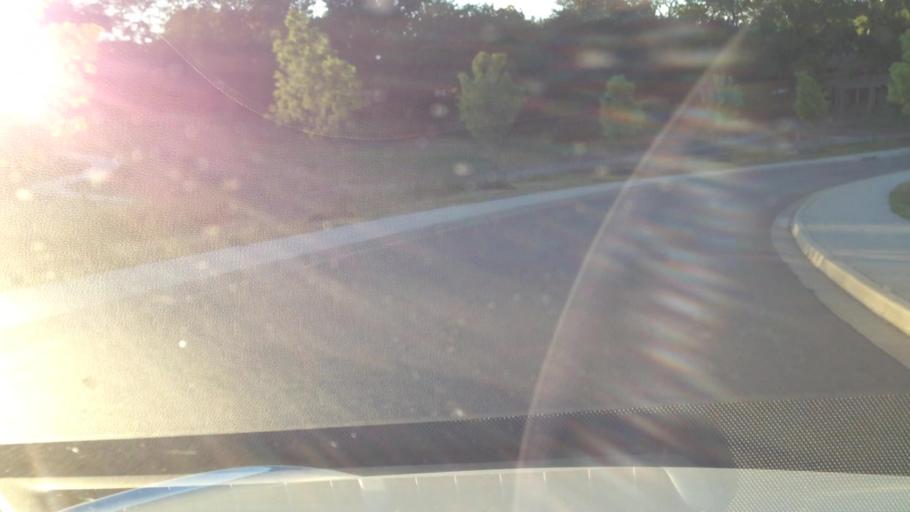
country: US
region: Kansas
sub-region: Douglas County
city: Lawrence
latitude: 38.9554
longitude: -95.2936
